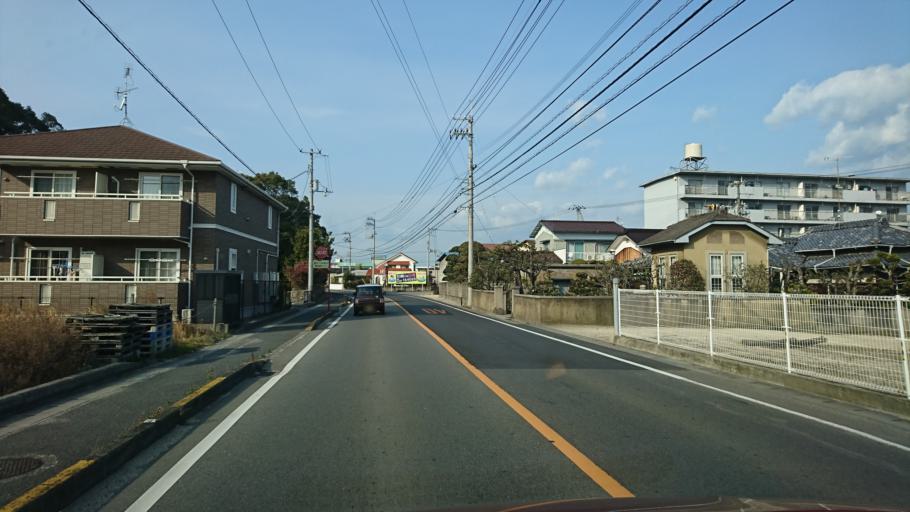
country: JP
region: Ehime
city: Saijo
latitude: 34.0336
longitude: 133.0351
